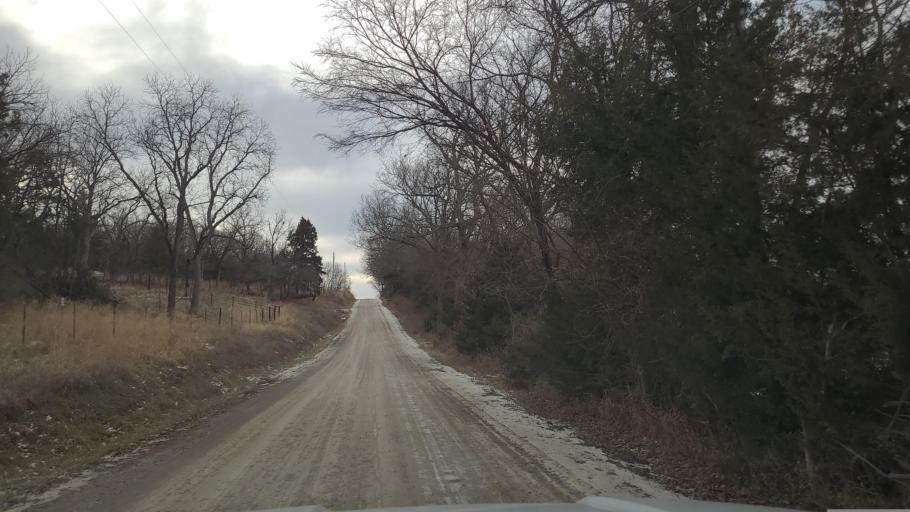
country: US
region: Kansas
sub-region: Shawnee County
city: Topeka
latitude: 39.0499
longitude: -95.4737
